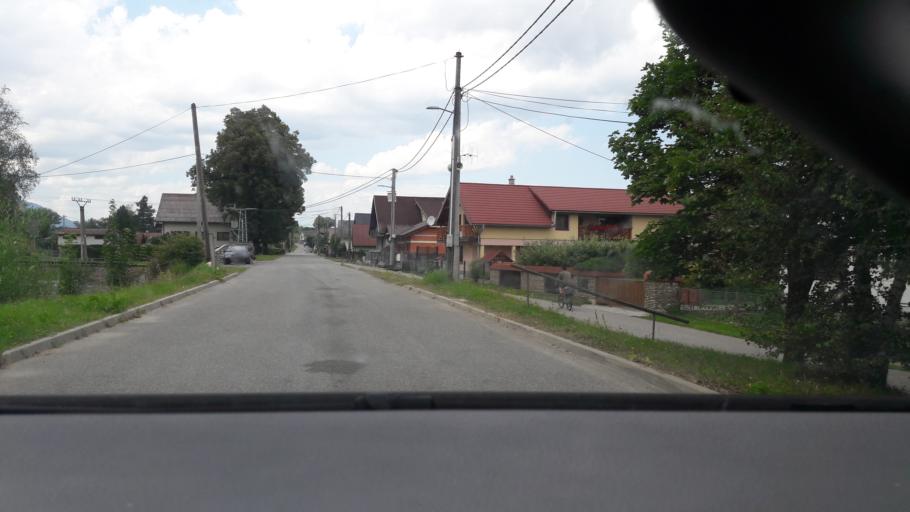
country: SK
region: Presovsky
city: Spisska Bela
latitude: 49.1742
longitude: 20.4571
